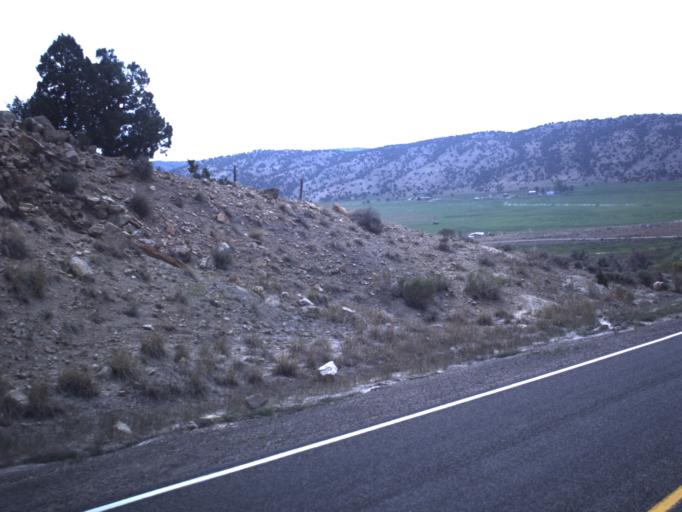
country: US
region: Utah
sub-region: Daggett County
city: Manila
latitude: 40.9546
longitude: -109.7129
